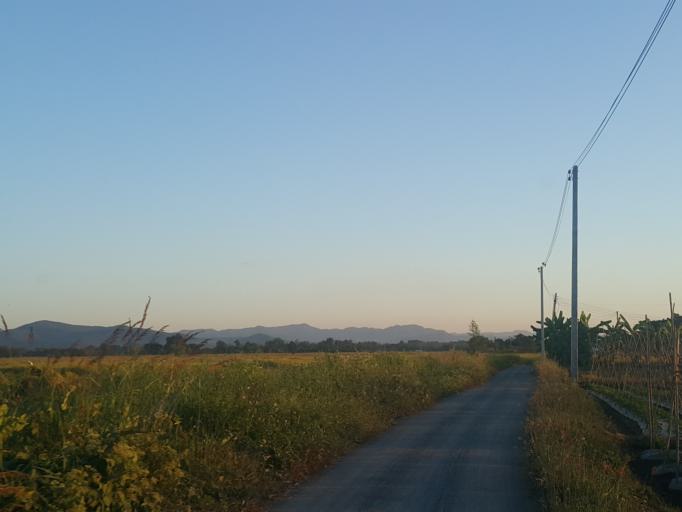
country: TH
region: Chiang Mai
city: San Kamphaeng
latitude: 18.8332
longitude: 99.1520
